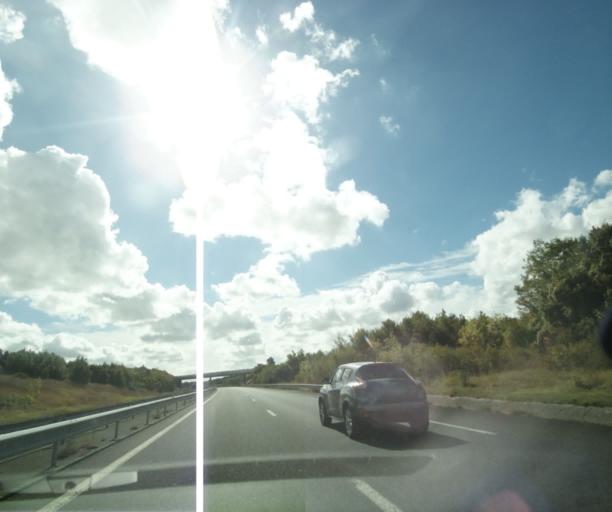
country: FR
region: Poitou-Charentes
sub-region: Departement de la Charente-Maritime
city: Saint-Savinien
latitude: 45.8555
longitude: -0.7272
